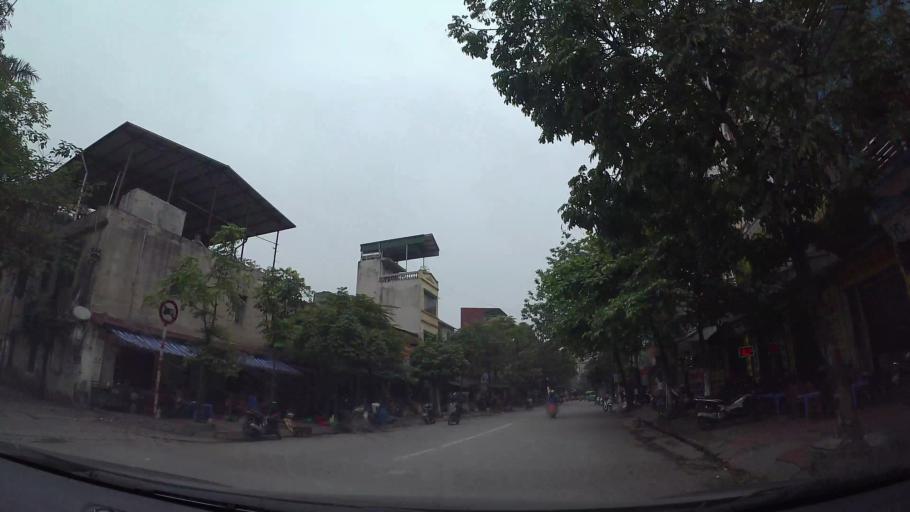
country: VN
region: Ha Noi
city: Hai BaTrung
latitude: 20.9875
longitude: 105.8591
